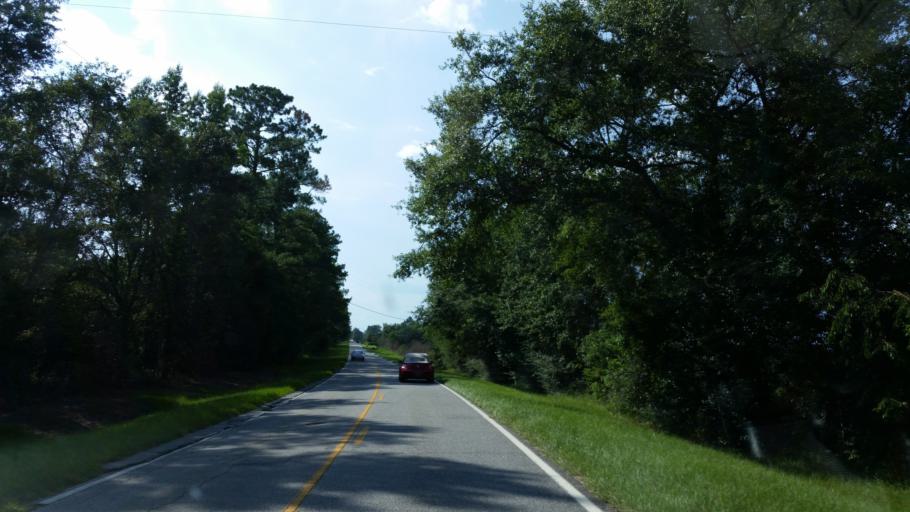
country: US
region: Georgia
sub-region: Lowndes County
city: Hahira
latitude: 30.9162
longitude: -83.3867
